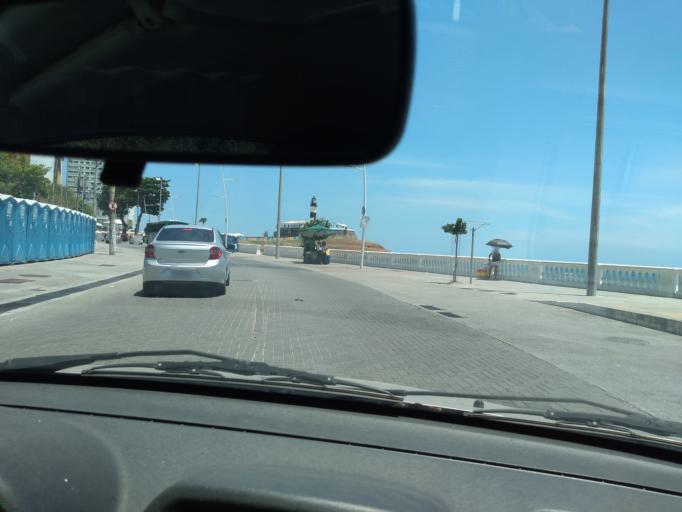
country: BR
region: Bahia
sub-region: Salvador
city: Salvador
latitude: -13.0066
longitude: -38.5331
